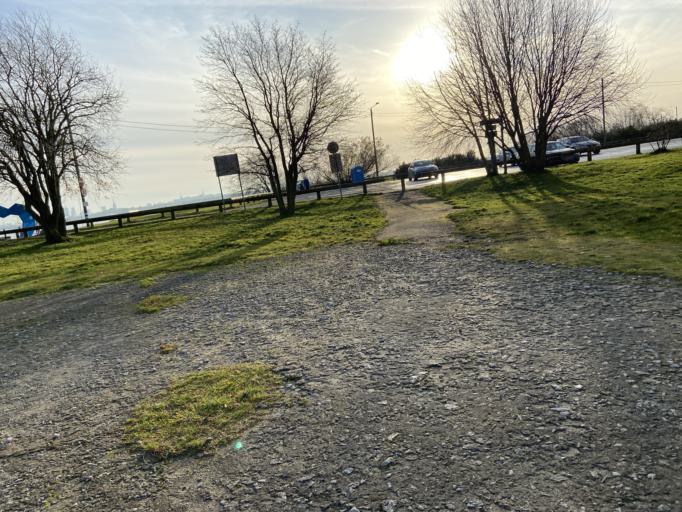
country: EE
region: Harju
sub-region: Tallinna linn
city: Tallinn
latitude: 59.4734
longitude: 24.7228
